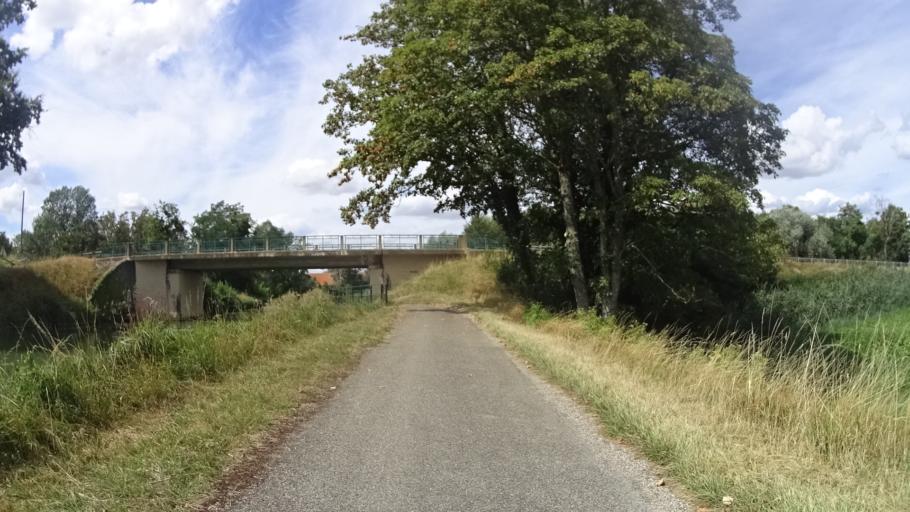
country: FR
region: Bourgogne
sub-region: Departement de la Cote-d'Or
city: Saint-Jean-de-Losne
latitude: 47.1006
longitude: 5.3180
